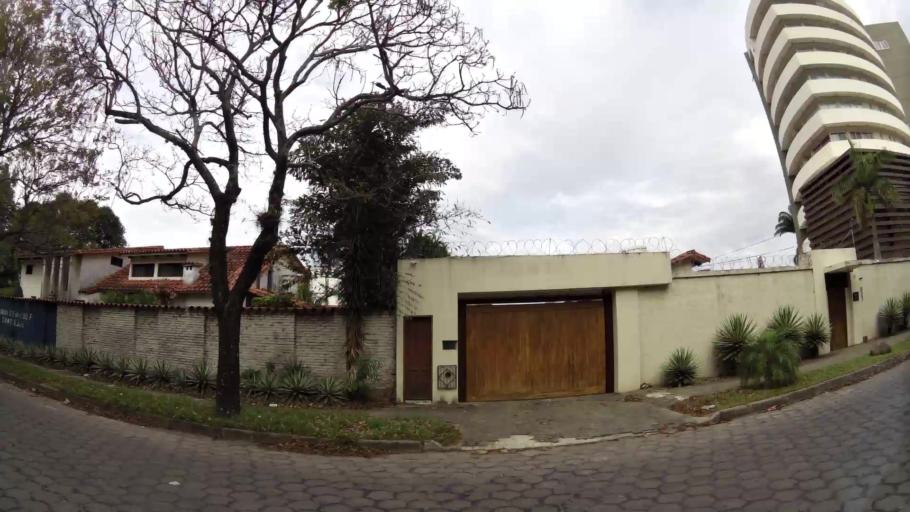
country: BO
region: Santa Cruz
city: Santa Cruz de la Sierra
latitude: -17.7931
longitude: -63.1967
